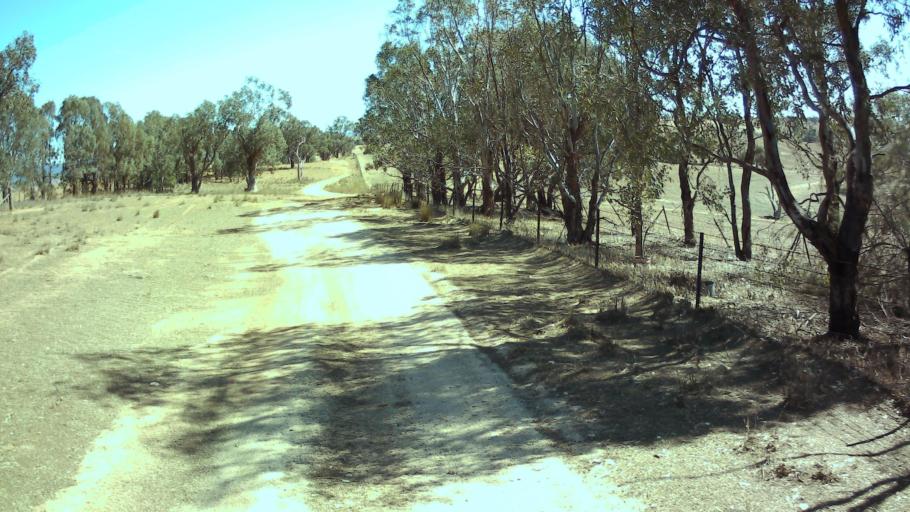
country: AU
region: New South Wales
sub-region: Weddin
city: Grenfell
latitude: -33.9952
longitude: 148.4364
